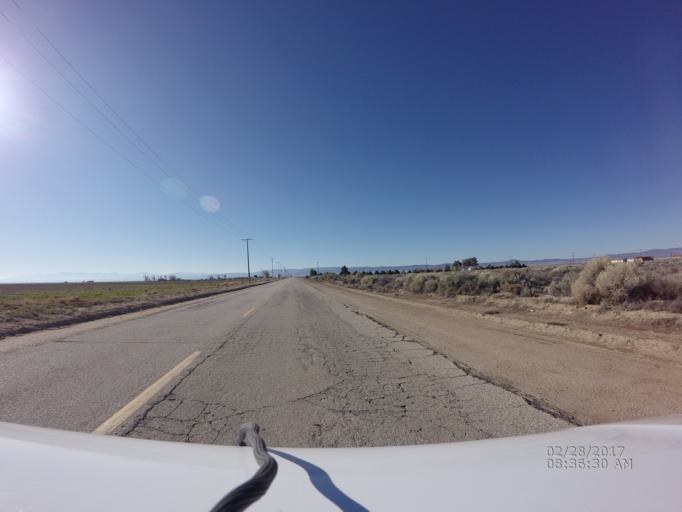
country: US
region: California
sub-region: Kern County
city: Rosamond
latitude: 34.8018
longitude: -118.2376
